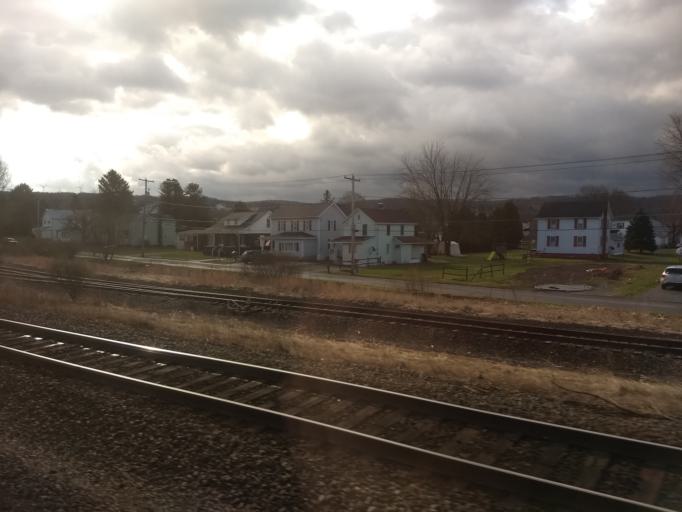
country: US
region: Pennsylvania
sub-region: Cambria County
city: Portage
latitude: 40.3892
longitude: -78.6787
